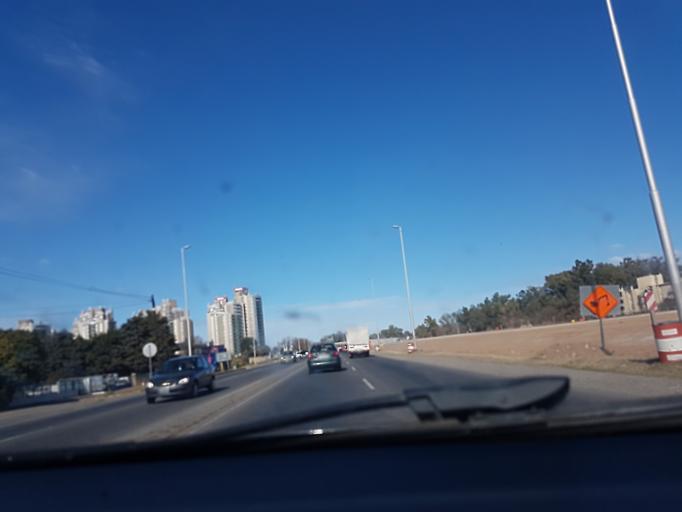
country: AR
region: Cordoba
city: La Calera
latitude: -31.3880
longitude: -64.2626
